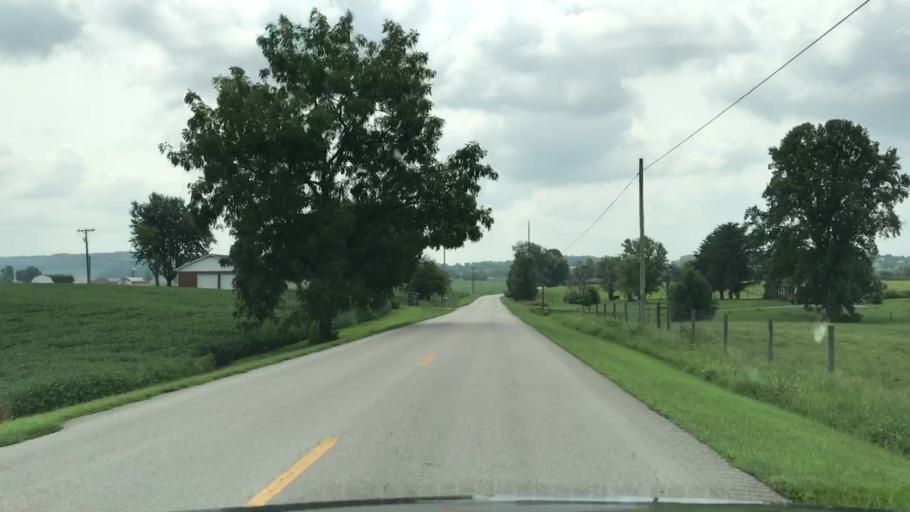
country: US
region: Kentucky
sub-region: Barren County
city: Cave City
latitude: 37.1013
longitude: -85.9771
